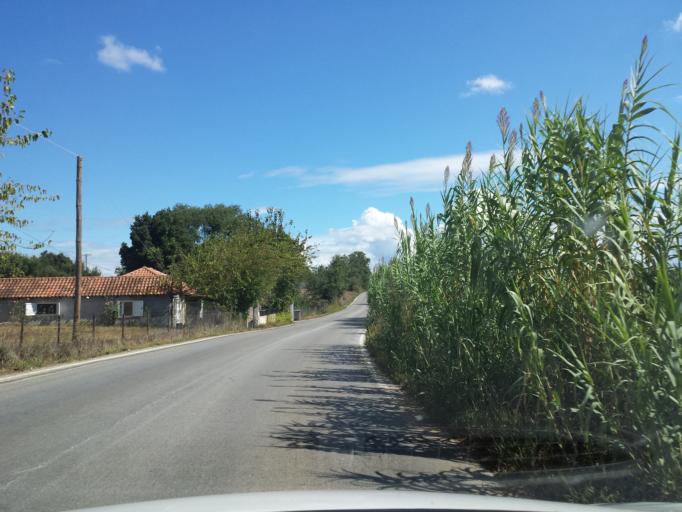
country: GR
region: Peloponnese
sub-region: Nomos Messinias
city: Vlakhopoulon
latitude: 36.9834
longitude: 21.8228
